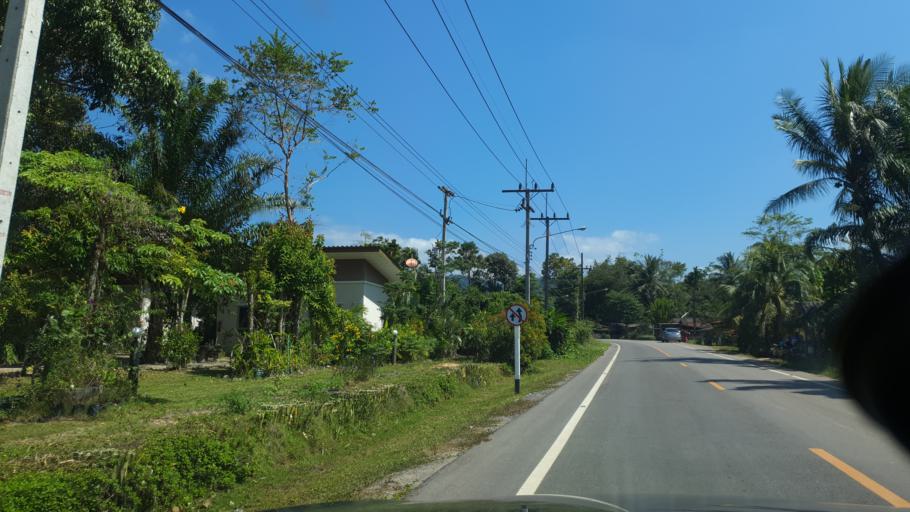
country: TH
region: Krabi
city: Khlong Thom
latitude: 7.9204
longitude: 99.2546
